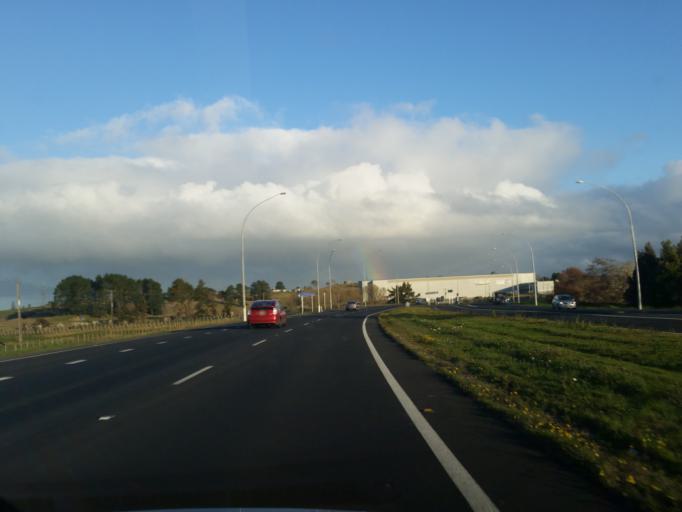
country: NZ
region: Waikato
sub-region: Waikato District
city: Te Kauwhata
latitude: -37.3079
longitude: 175.0671
